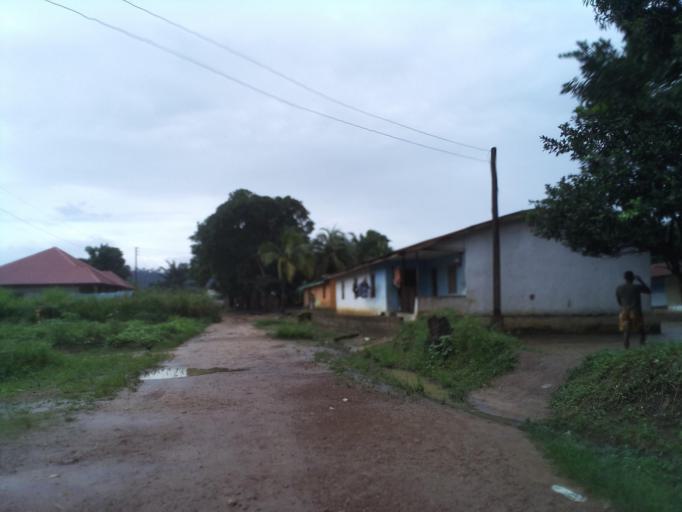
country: SL
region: Eastern Province
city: Kenema
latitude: 7.8525
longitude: -11.1980
